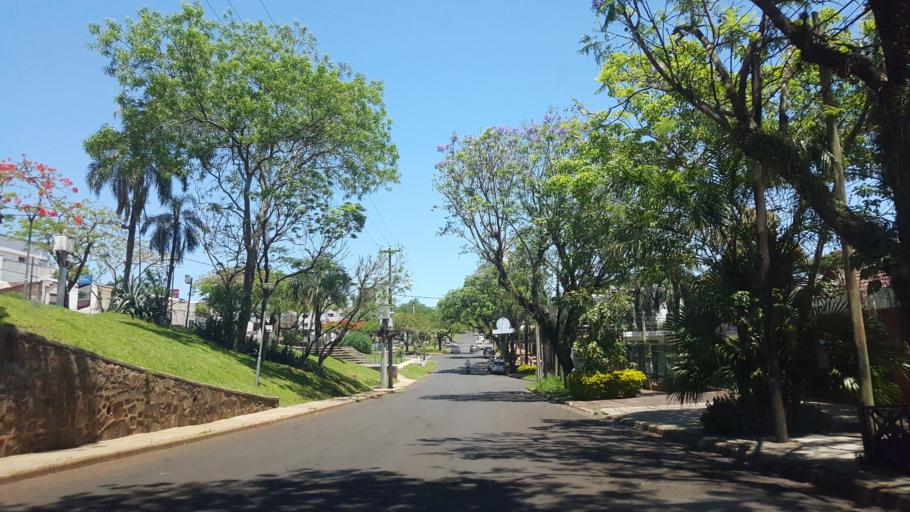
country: AR
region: Misiones
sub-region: Departamento de Capital
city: Posadas
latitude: -27.3624
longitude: -55.9008
